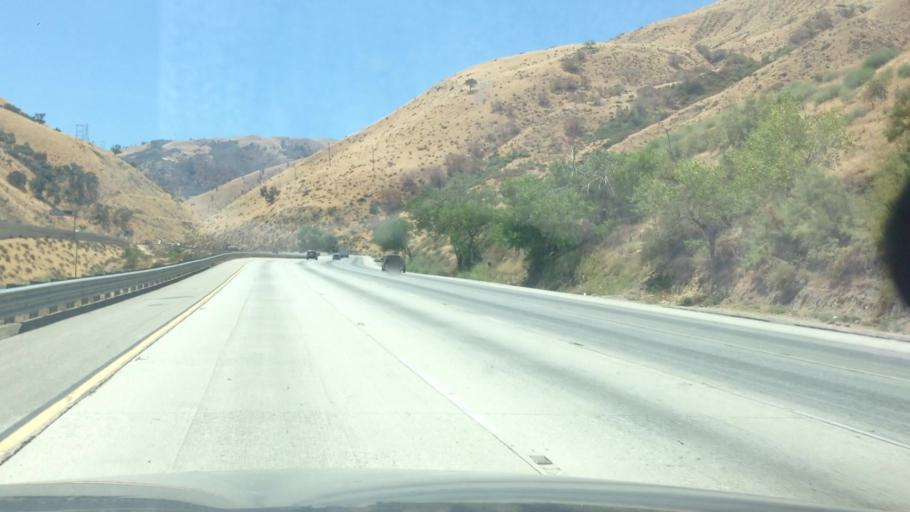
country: US
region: California
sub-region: Kern County
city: Lebec
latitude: 34.9204
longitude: -118.9253
